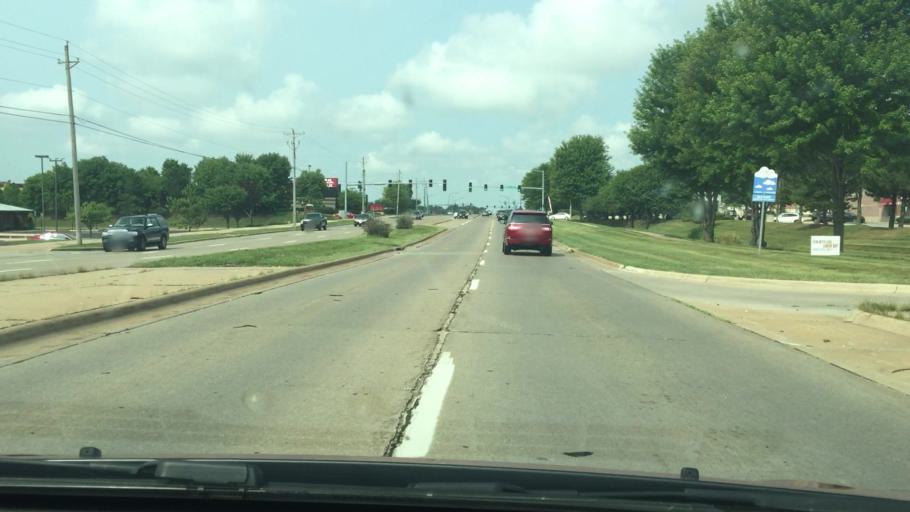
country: US
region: Iowa
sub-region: Scott County
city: Bettendorf
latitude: 41.5750
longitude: -90.5150
